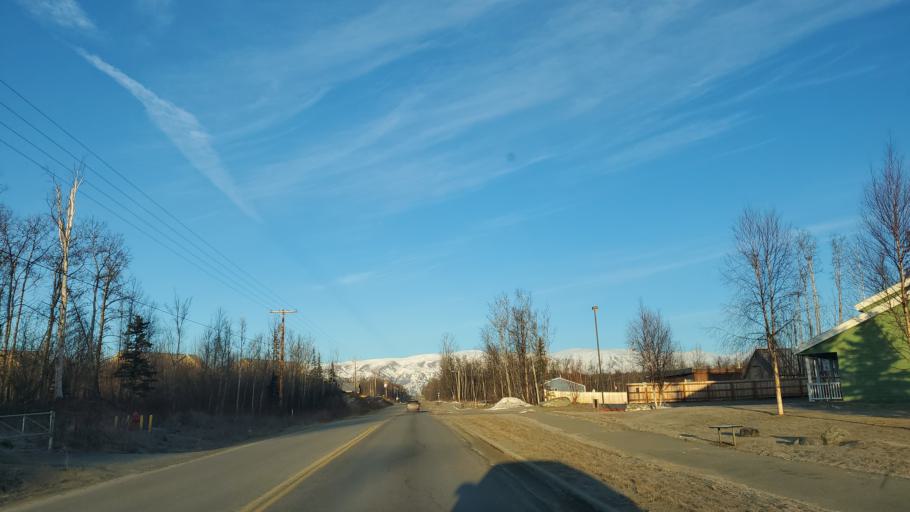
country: US
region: Alaska
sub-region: Matanuska-Susitna Borough
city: Wasilla
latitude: 61.5893
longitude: -149.4508
